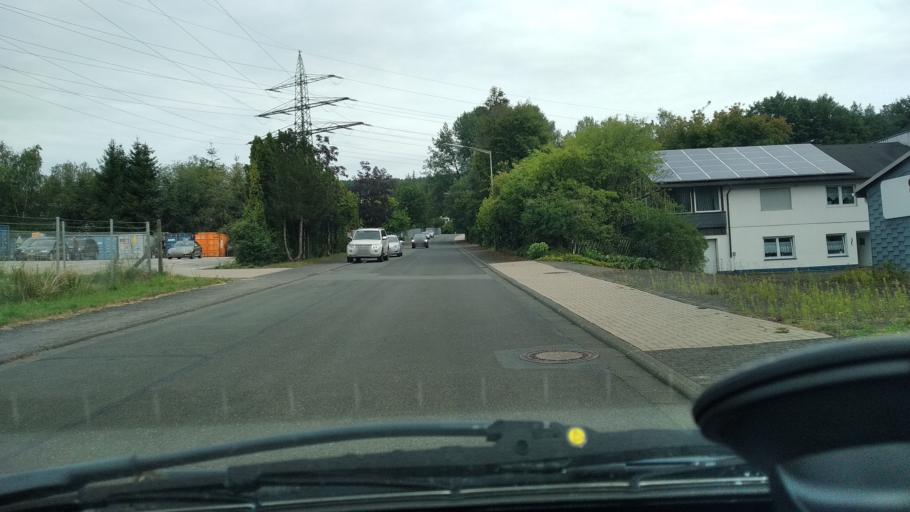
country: DE
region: North Rhine-Westphalia
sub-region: Regierungsbezirk Arnsberg
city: Burbach
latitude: 50.7521
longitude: 8.0996
